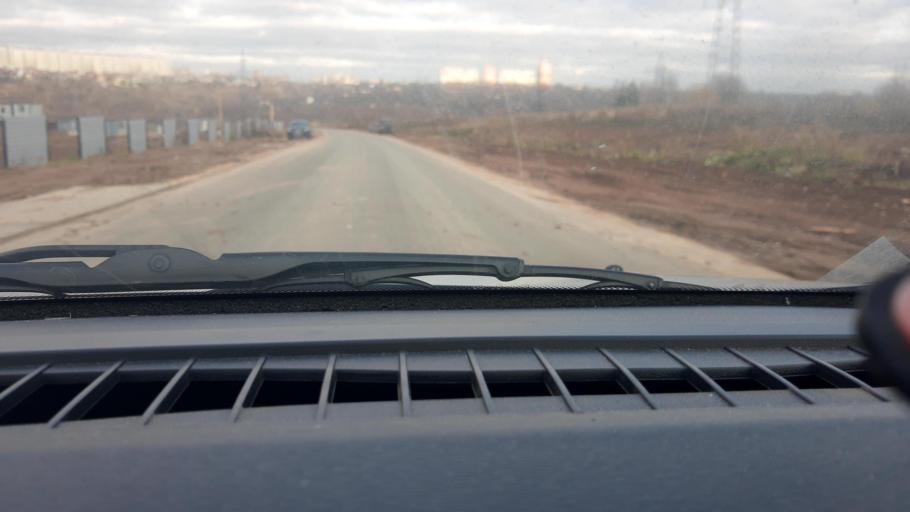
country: RU
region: Nizjnij Novgorod
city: Afonino
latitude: 56.2712
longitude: 44.0508
